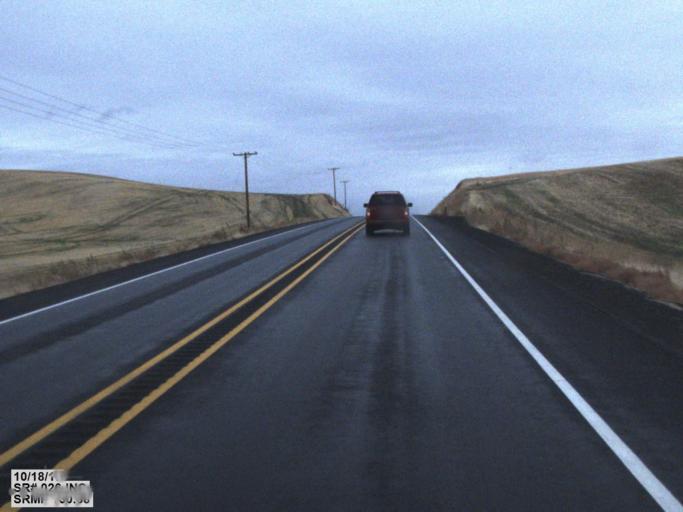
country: US
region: Washington
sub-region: Whitman County
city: Colfax
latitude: 46.8714
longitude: -117.4105
